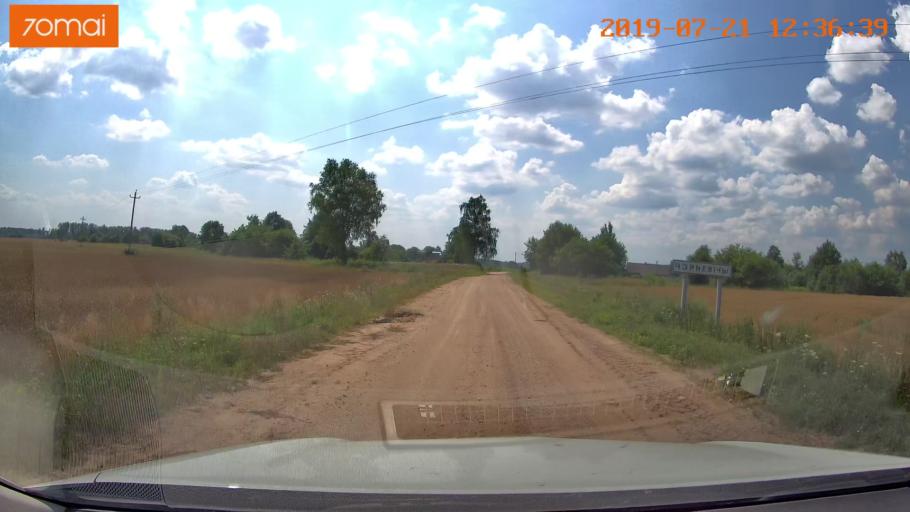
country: BY
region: Grodnenskaya
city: Lyubcha
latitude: 53.8685
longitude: 26.0027
